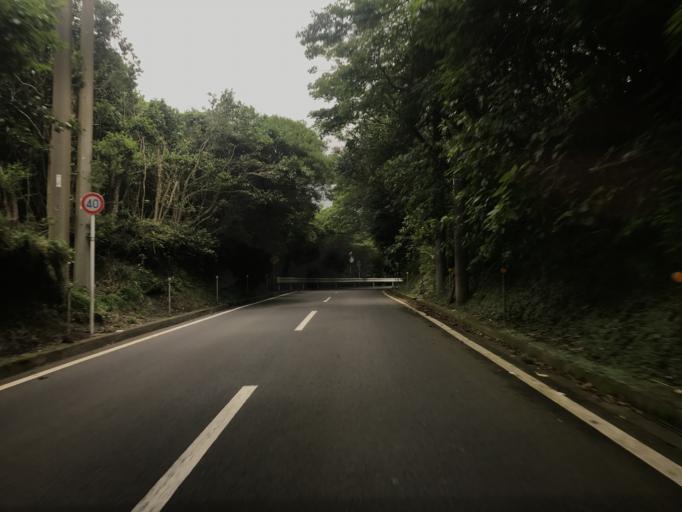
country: JP
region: Shizuoka
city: Ito
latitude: 34.7592
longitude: 139.3932
